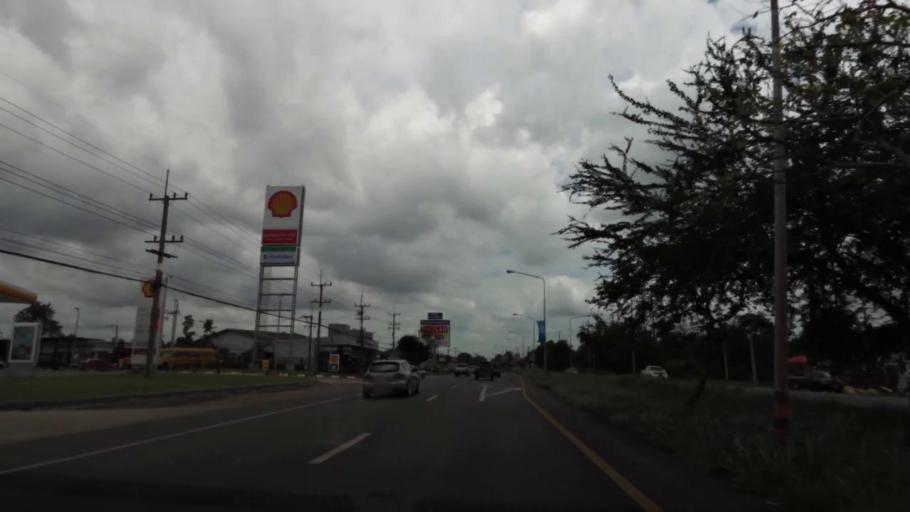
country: TH
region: Rayong
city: Klaeng
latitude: 12.7830
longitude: 101.6894
